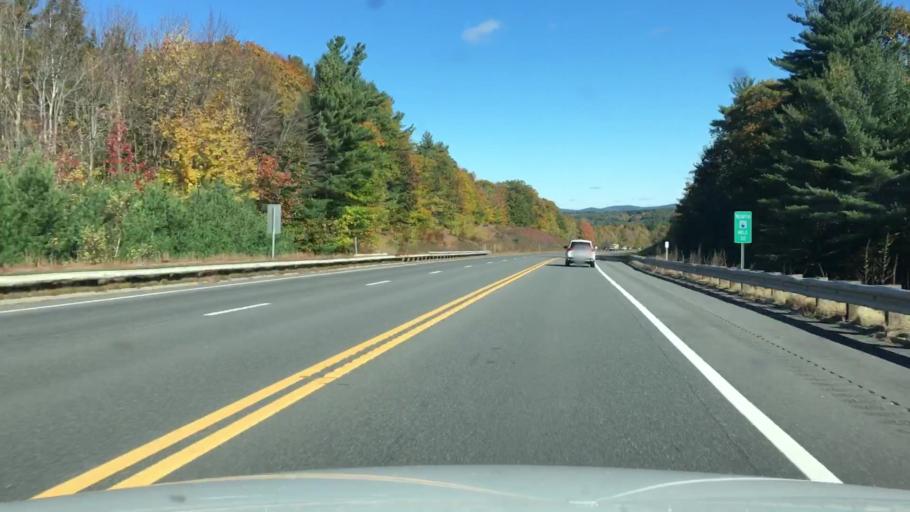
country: US
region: New Hampshire
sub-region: Strafford County
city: Farmington
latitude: 43.4385
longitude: -71.0067
